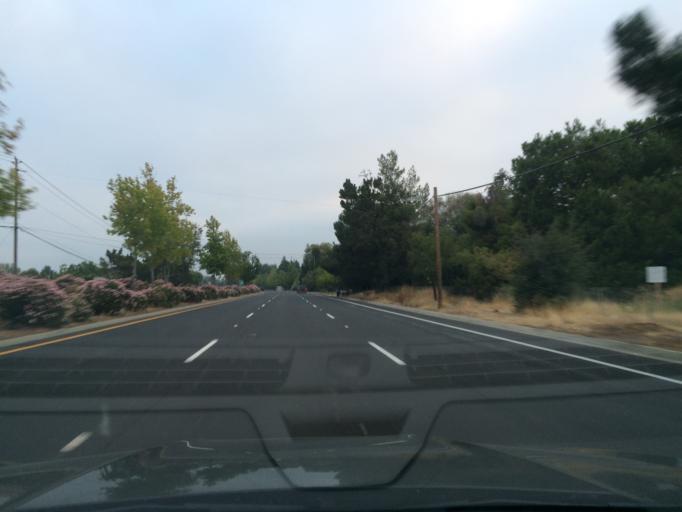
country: US
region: California
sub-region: Santa Clara County
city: Seven Trees
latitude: 37.2321
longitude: -121.8713
